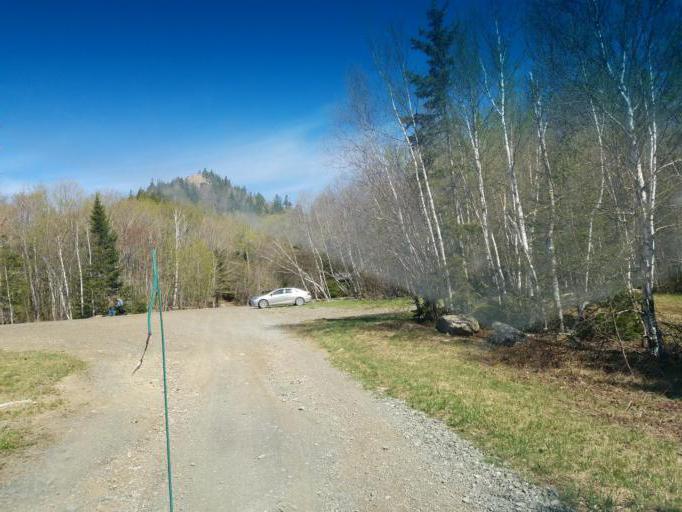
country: US
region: Maine
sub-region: Aroostook County
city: Presque Isle
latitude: 46.6644
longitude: -68.2286
